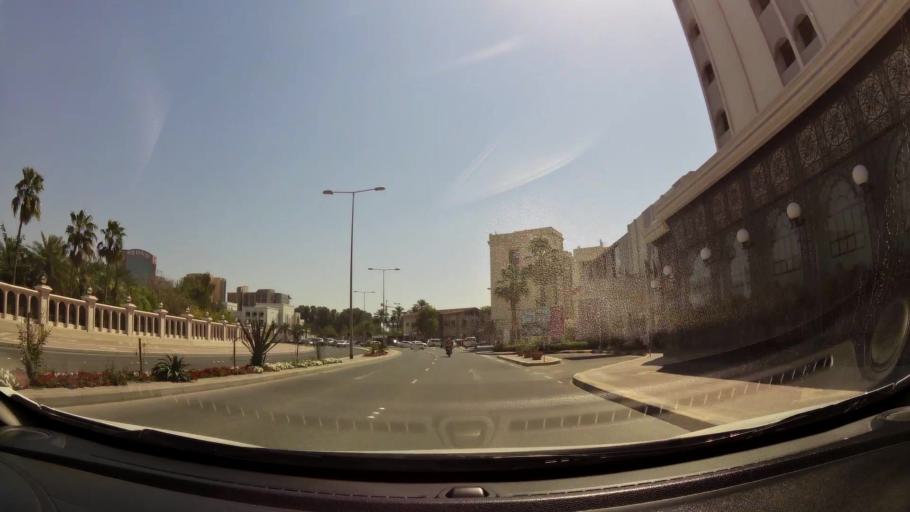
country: BH
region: Manama
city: Manama
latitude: 26.2175
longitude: 50.5907
